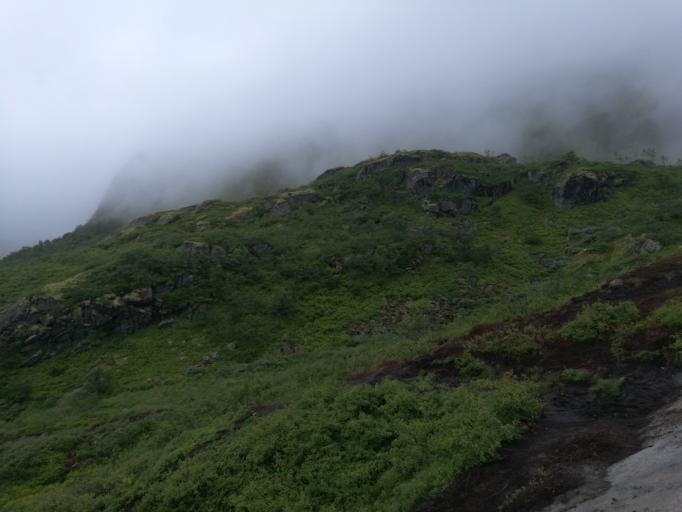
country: NO
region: Nordland
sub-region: Vagan
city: Svolvaer
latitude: 68.2489
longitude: 14.5881
